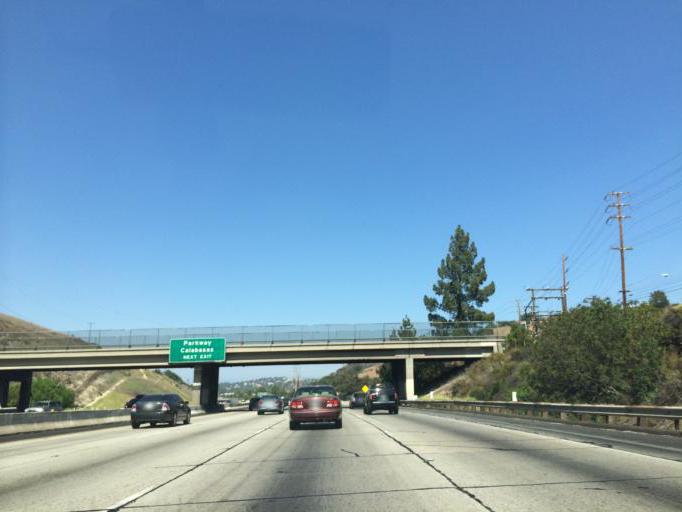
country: US
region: California
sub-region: Los Angeles County
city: Hidden Hills
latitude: 34.1495
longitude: -118.6656
